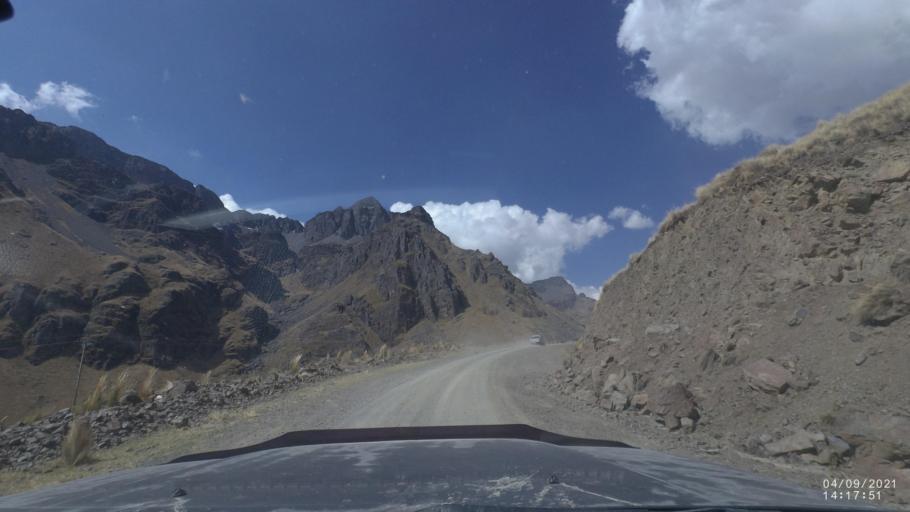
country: BO
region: Cochabamba
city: Sipe Sipe
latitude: -17.2303
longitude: -66.4325
